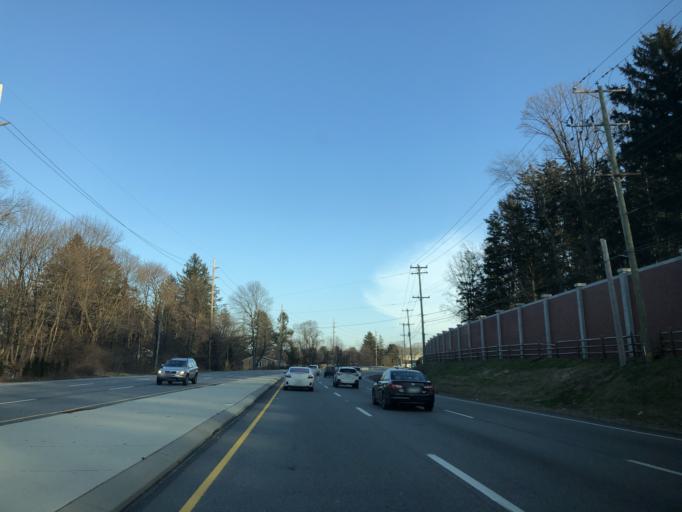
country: US
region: Pennsylvania
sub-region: Chester County
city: Exton
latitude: 40.0559
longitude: -75.6460
